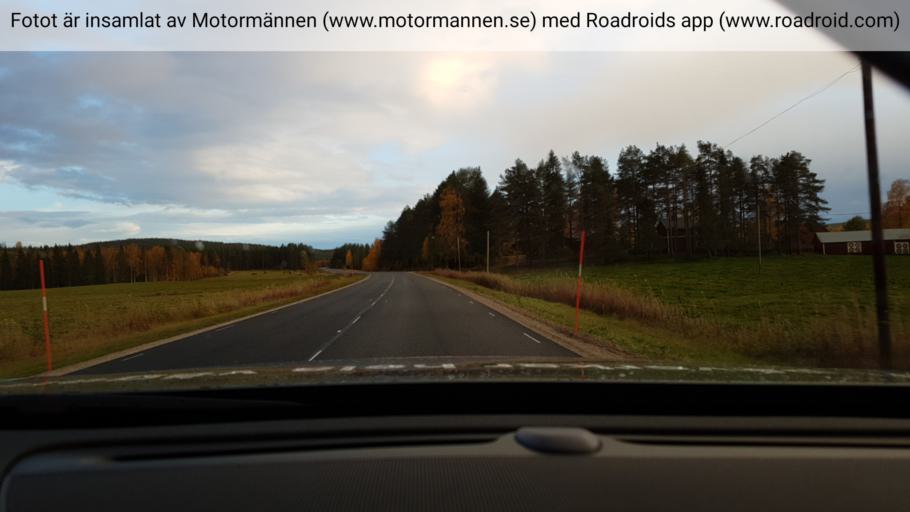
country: SE
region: Norrbotten
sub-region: Overkalix Kommun
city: OEverkalix
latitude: 66.4259
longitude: 22.7967
